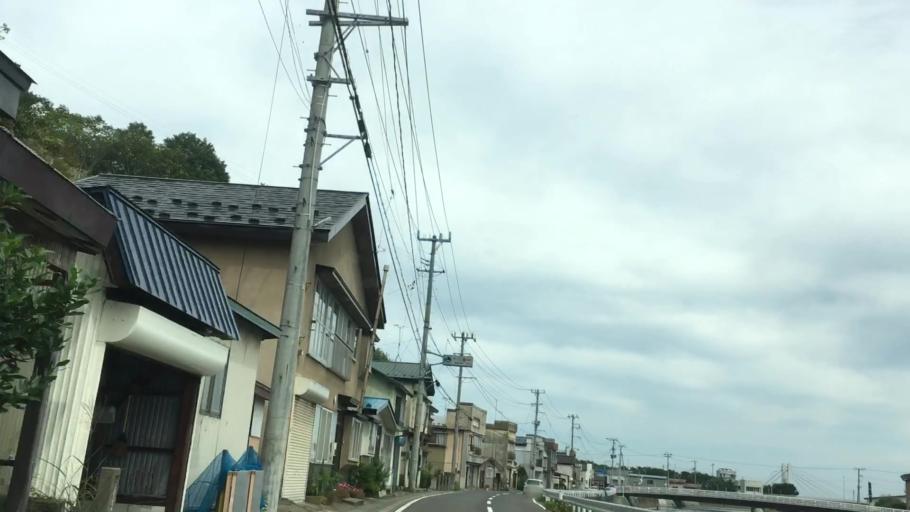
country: JP
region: Aomori
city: Shimokizukuri
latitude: 40.7755
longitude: 140.2164
